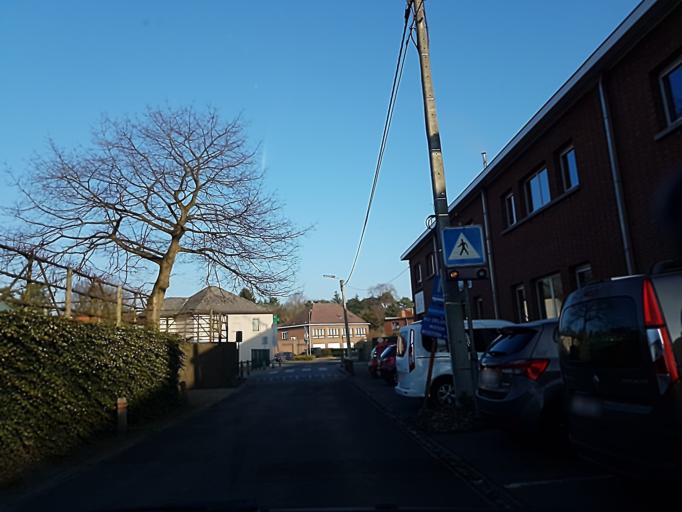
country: BE
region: Flanders
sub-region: Provincie Vlaams-Brabant
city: Tremelo
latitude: 50.9940
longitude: 4.6851
